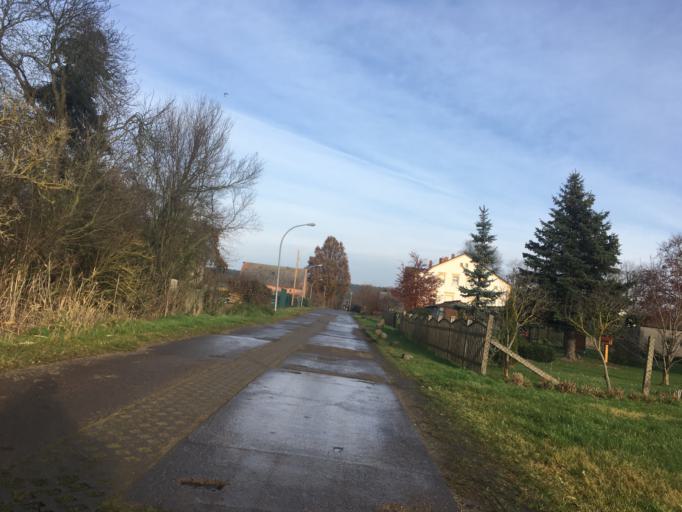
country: DE
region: Brandenburg
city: Bad Freienwalde
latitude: 52.8067
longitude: 14.0109
